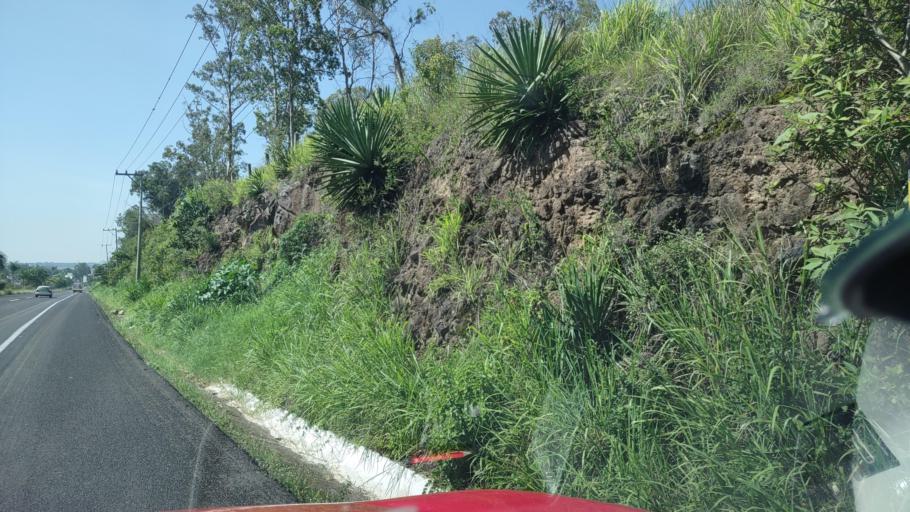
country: MX
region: Veracruz
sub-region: Emiliano Zapata
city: Dos Rios
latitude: 19.4985
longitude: -96.8219
